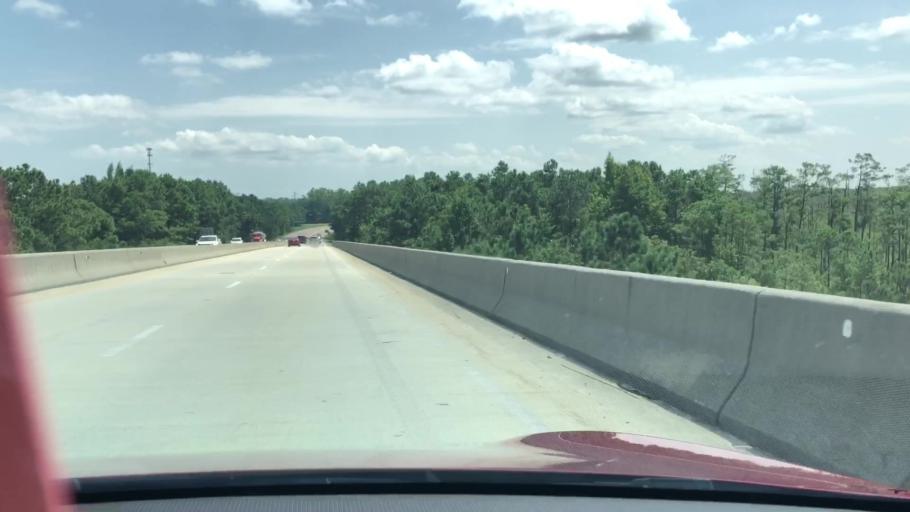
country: US
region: North Carolina
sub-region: Currituck County
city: Currituck
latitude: 36.3393
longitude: -75.9528
